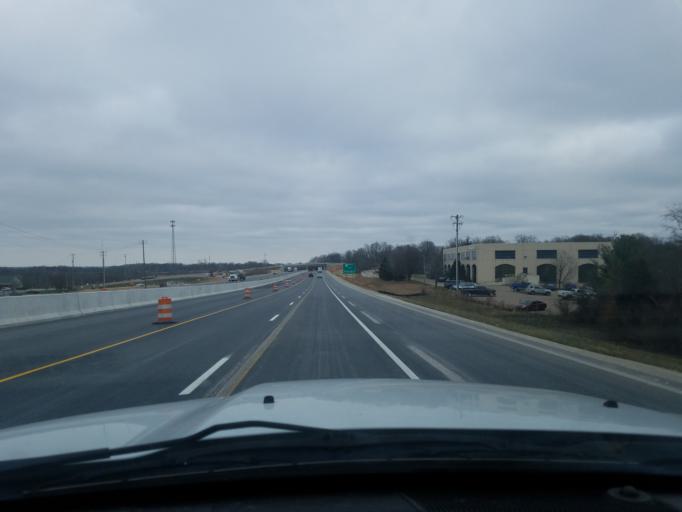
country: US
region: Indiana
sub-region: Monroe County
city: Bloomington
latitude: 39.1751
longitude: -86.5643
